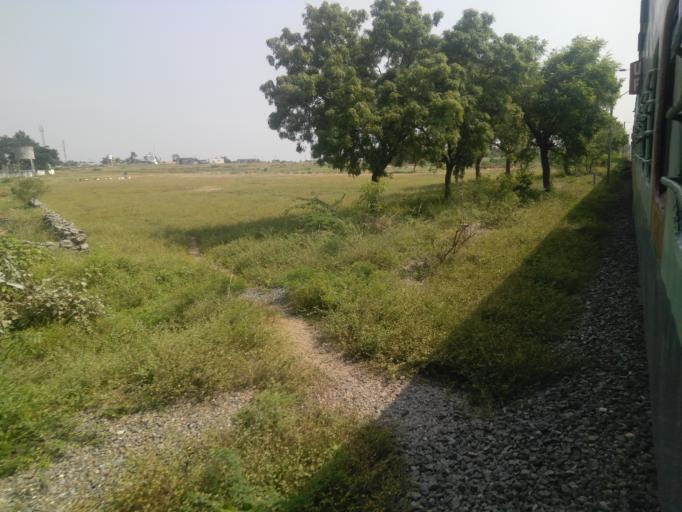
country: IN
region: Tamil Nadu
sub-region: Coimbatore
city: Mettupalayam
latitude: 11.2768
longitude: 76.9427
